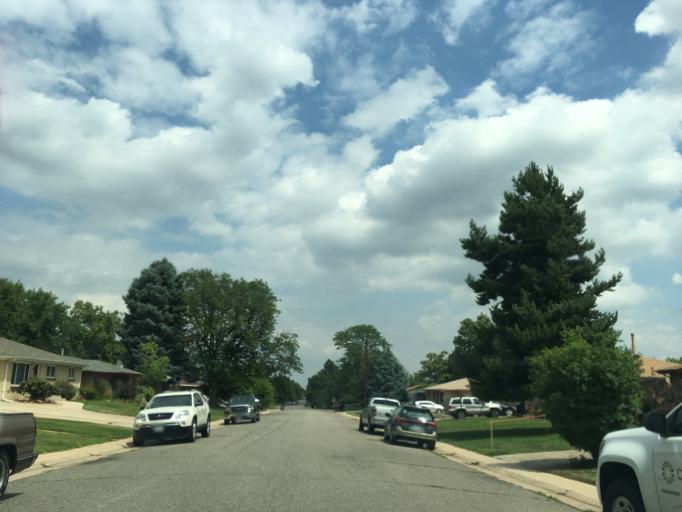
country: US
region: Colorado
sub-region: Arapahoe County
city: Sheridan
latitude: 39.6661
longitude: -105.0271
